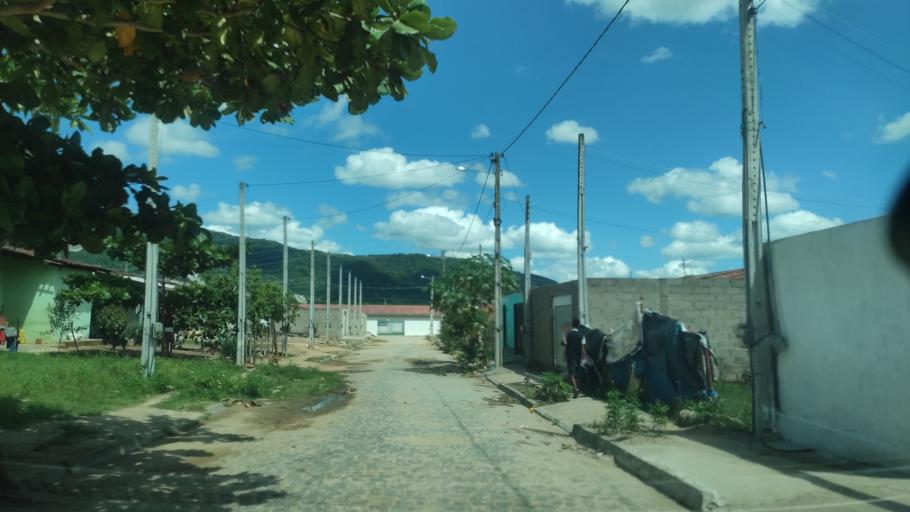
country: BR
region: Alagoas
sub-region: Uniao Dos Palmares
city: Uniao dos Palmares
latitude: -9.1447
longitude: -36.0024
